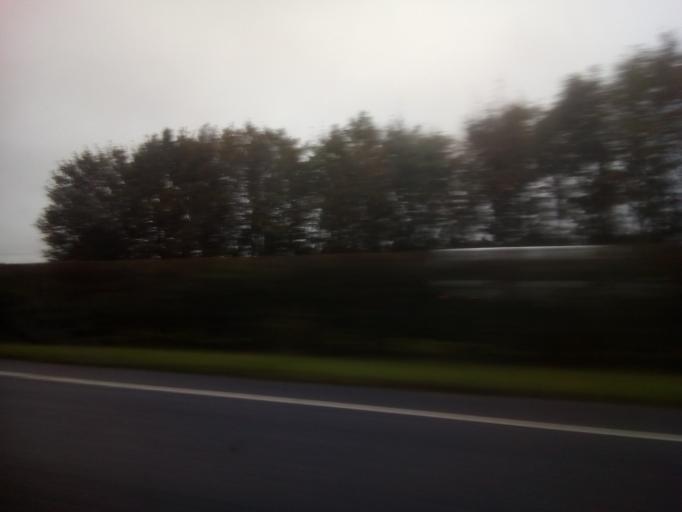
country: IE
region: Leinster
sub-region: An Iarmhi
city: An Muileann gCearr
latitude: 53.5194
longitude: -7.2871
